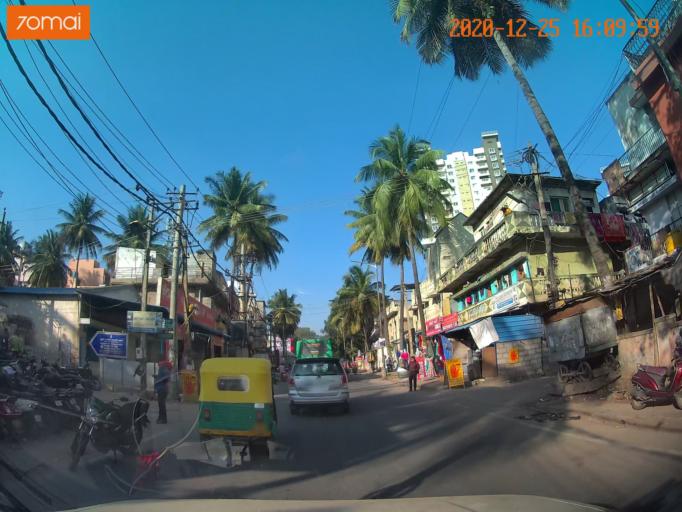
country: IN
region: Karnataka
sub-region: Bangalore Urban
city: Bangalore
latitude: 12.9014
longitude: 77.6272
